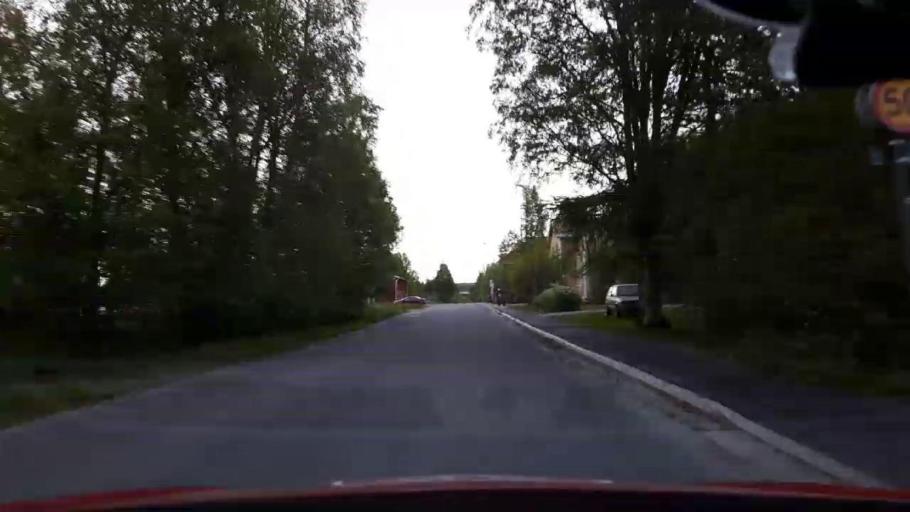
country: SE
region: Jaemtland
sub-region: OEstersunds Kommun
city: Ostersund
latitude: 62.9936
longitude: 14.5757
